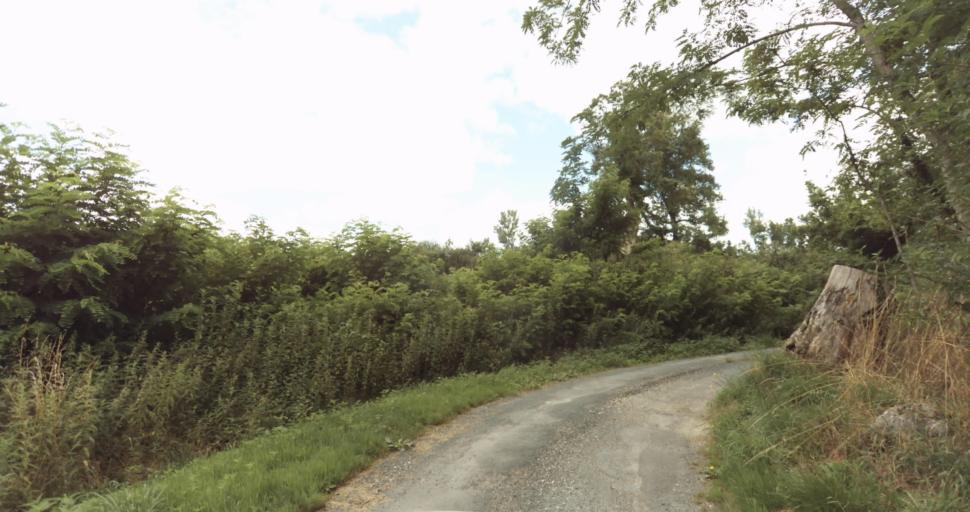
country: FR
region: Aquitaine
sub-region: Departement de la Gironde
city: Bazas
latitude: 44.4436
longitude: -0.2302
